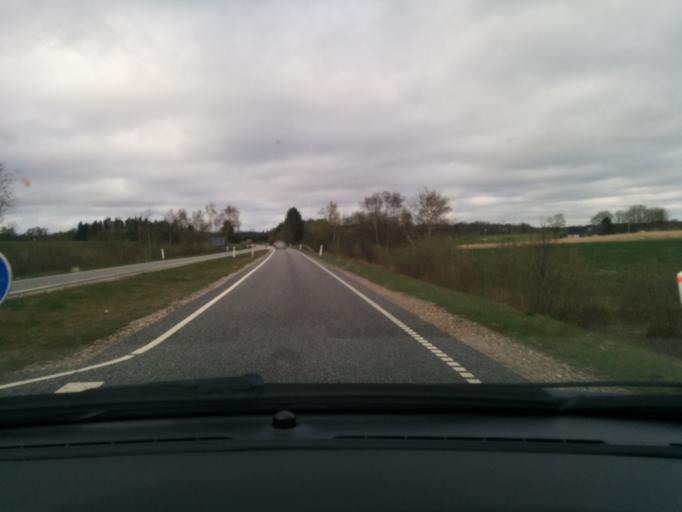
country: DK
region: Central Jutland
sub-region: Favrskov Kommune
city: Hammel
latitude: 56.2412
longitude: 9.8724
